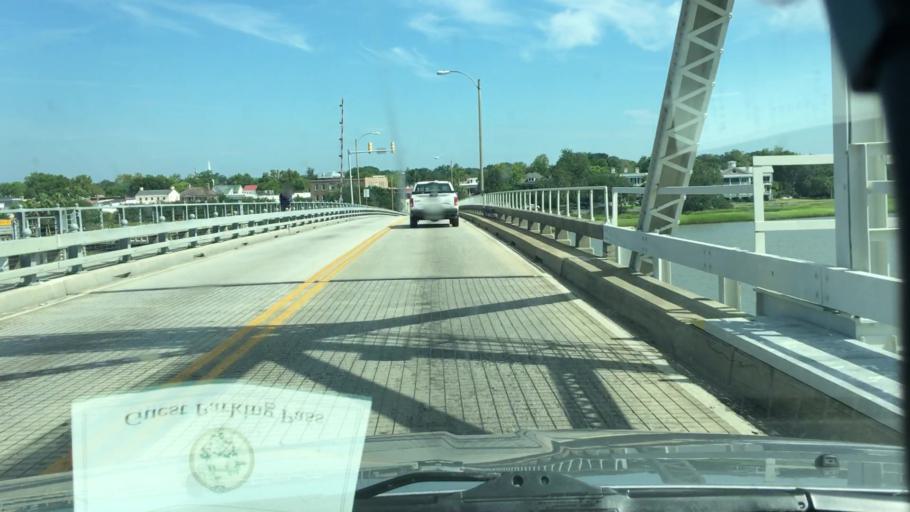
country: US
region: South Carolina
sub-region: Beaufort County
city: Beaufort
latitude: 32.4278
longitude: -80.6692
